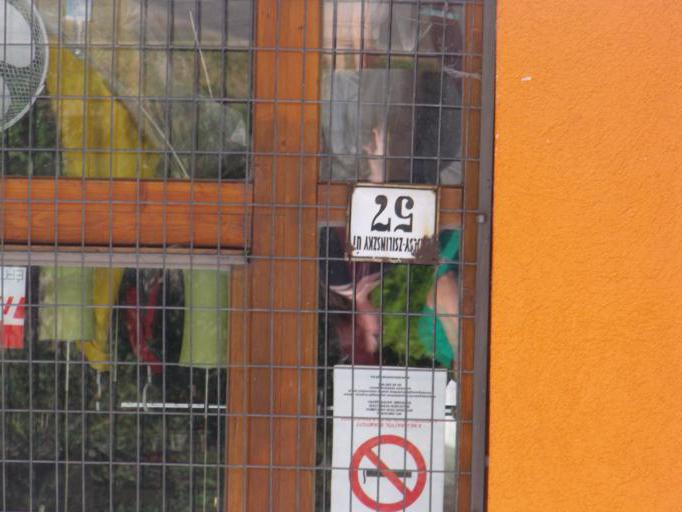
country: HU
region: Pest
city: Inarcs
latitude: 47.2582
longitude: 19.3332
